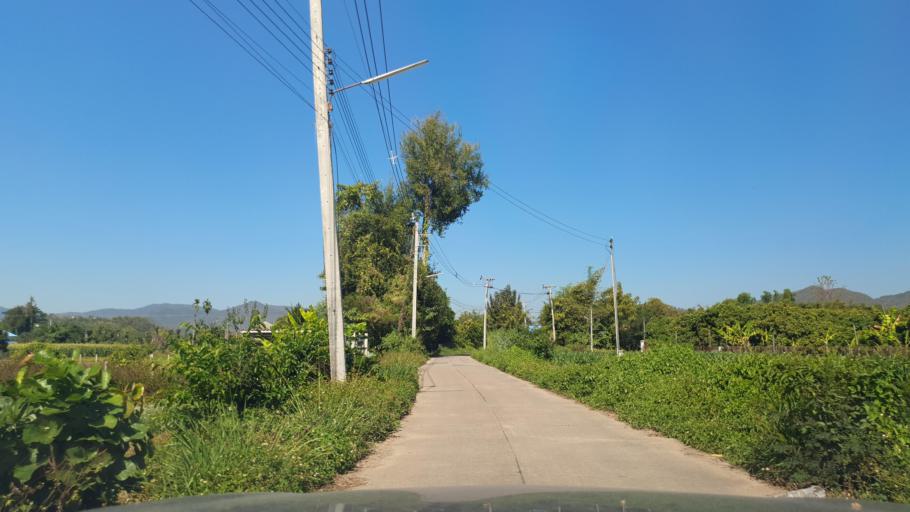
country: TH
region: Chiang Mai
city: Mae Wang
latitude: 18.6623
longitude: 98.8290
